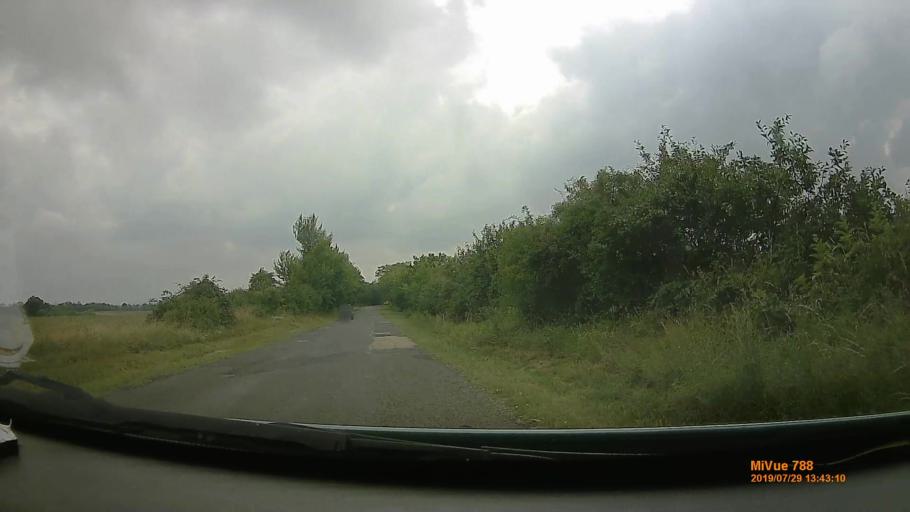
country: HU
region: Somogy
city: Balatonfoldvar
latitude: 46.8053
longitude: 17.9319
